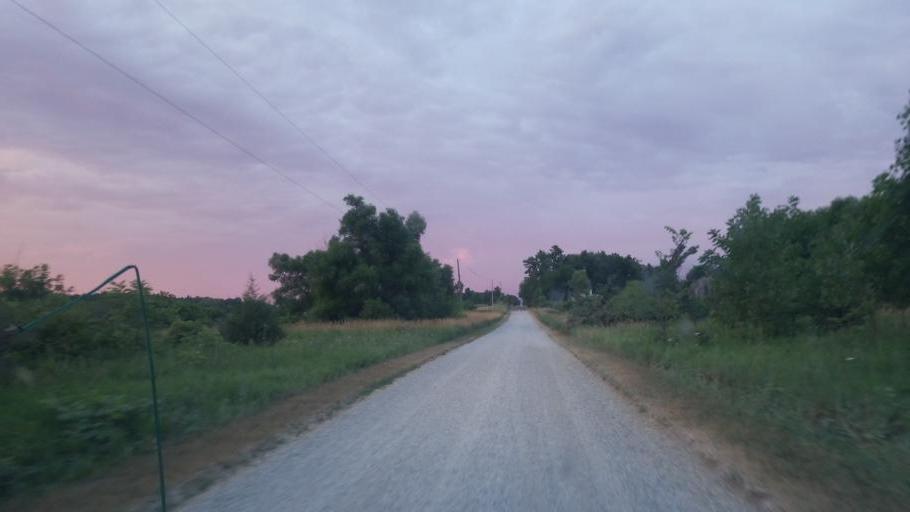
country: US
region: Ohio
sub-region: Defiance County
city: Hicksville
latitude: 41.3431
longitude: -84.8041
